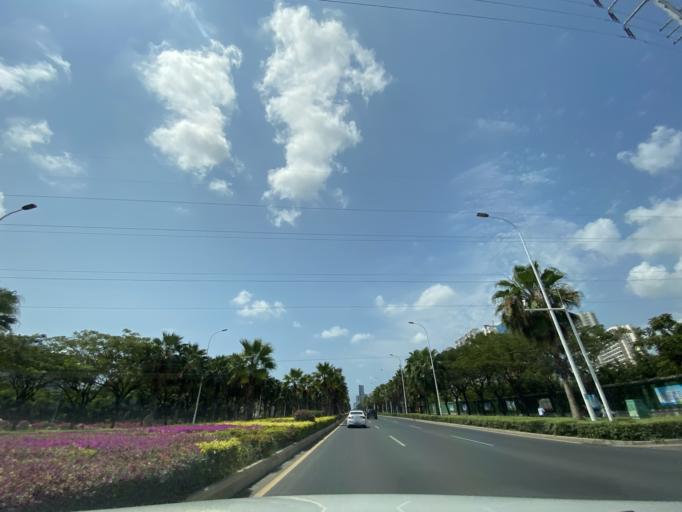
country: CN
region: Hainan
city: Sanya
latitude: 18.2878
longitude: 109.5215
